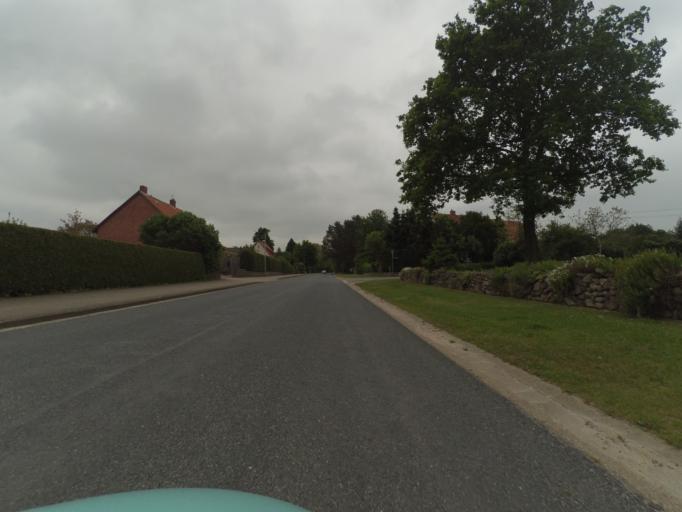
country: DE
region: Lower Saxony
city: Edemissen
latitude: 52.4273
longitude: 10.3052
